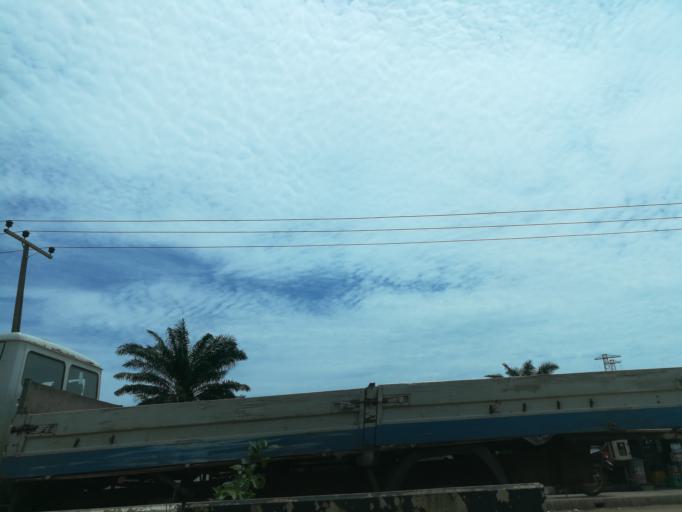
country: NG
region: Lagos
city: Ebute Ikorodu
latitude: 6.5976
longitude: 3.4995
